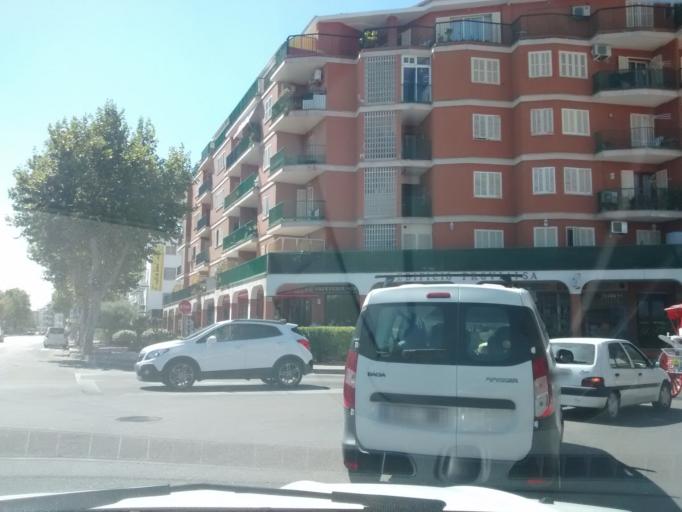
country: ES
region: Balearic Islands
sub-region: Illes Balears
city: Port d'Alcudia
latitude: 39.8444
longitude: 3.1327
